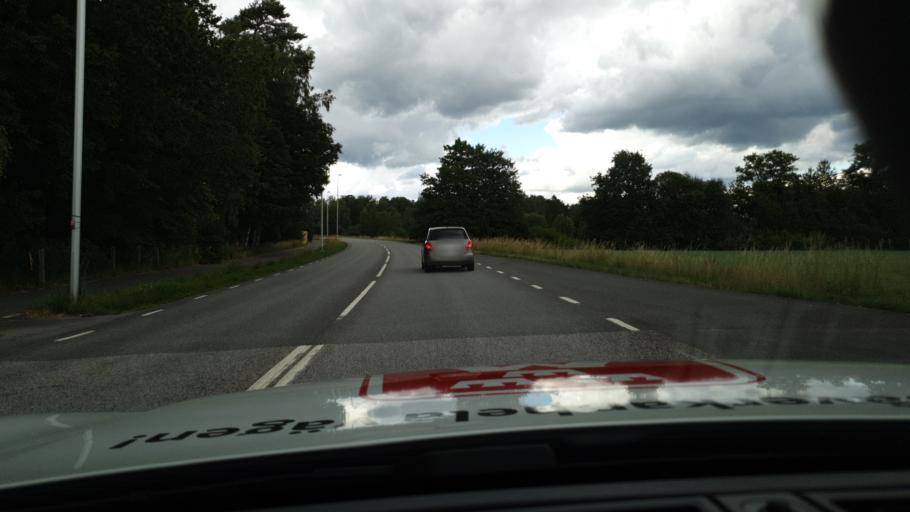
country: SE
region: Skane
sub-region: Hassleholms Kommun
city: Tormestorp
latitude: 56.1282
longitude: 13.7412
